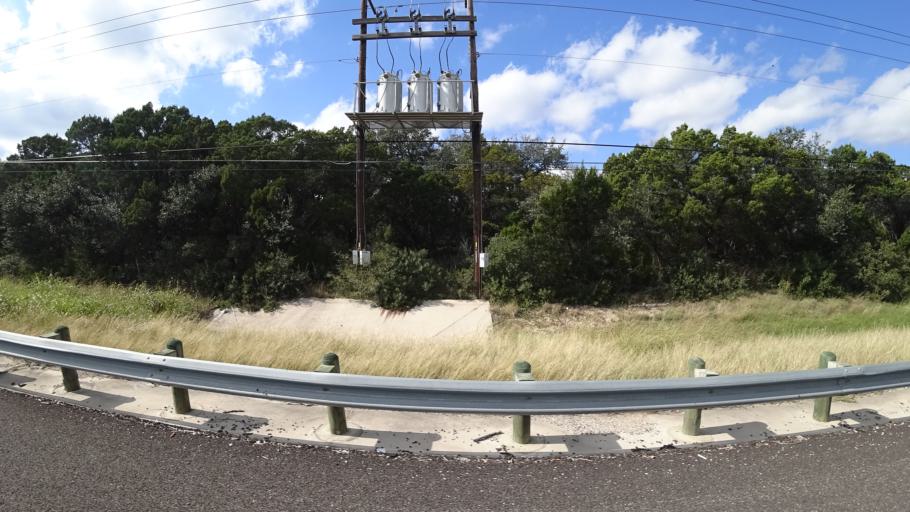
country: US
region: Texas
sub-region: Travis County
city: Bee Cave
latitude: 30.2843
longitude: -97.9168
